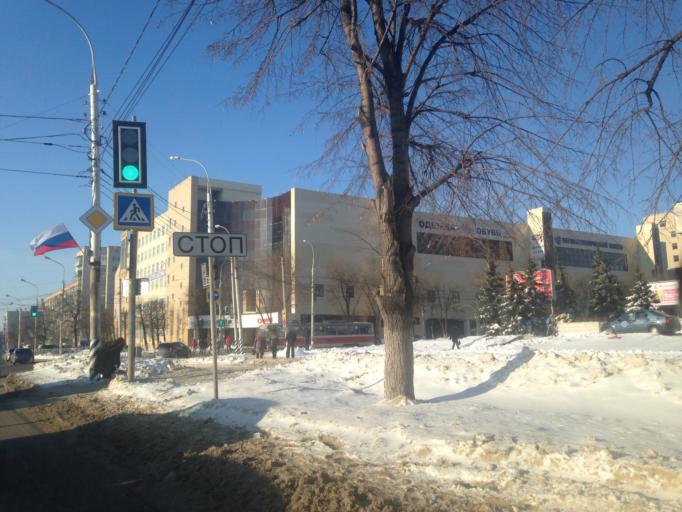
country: RU
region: Ulyanovsk
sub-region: Ulyanovskiy Rayon
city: Ulyanovsk
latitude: 54.3077
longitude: 48.3899
